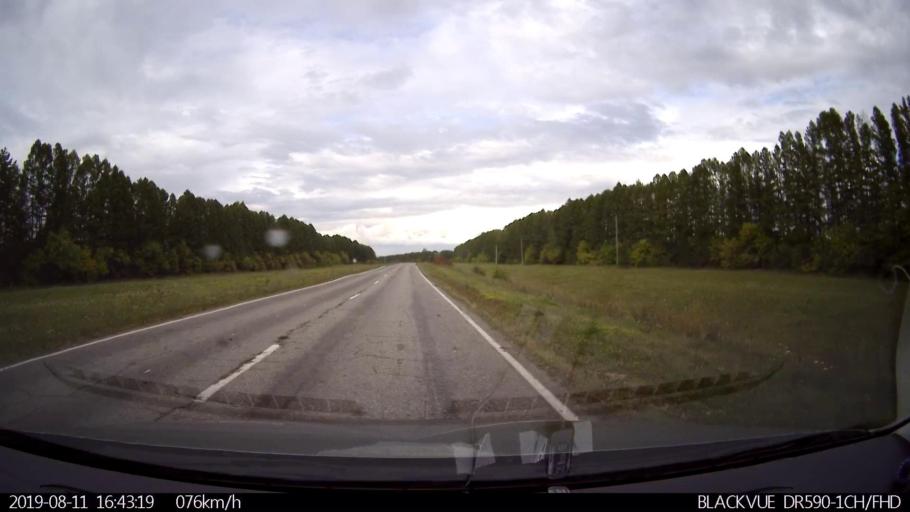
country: RU
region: Ulyanovsk
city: Mayna
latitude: 54.1678
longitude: 47.6707
